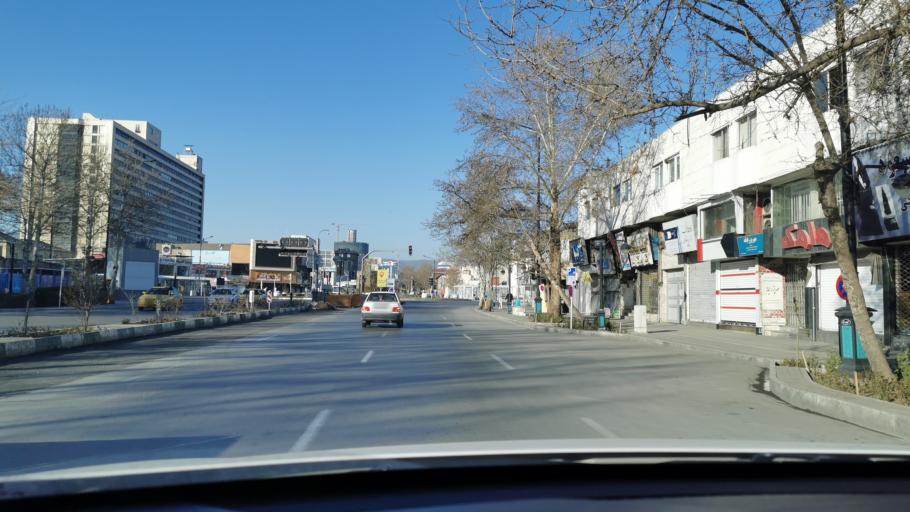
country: IR
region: Razavi Khorasan
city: Mashhad
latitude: 36.2916
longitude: 59.5871
